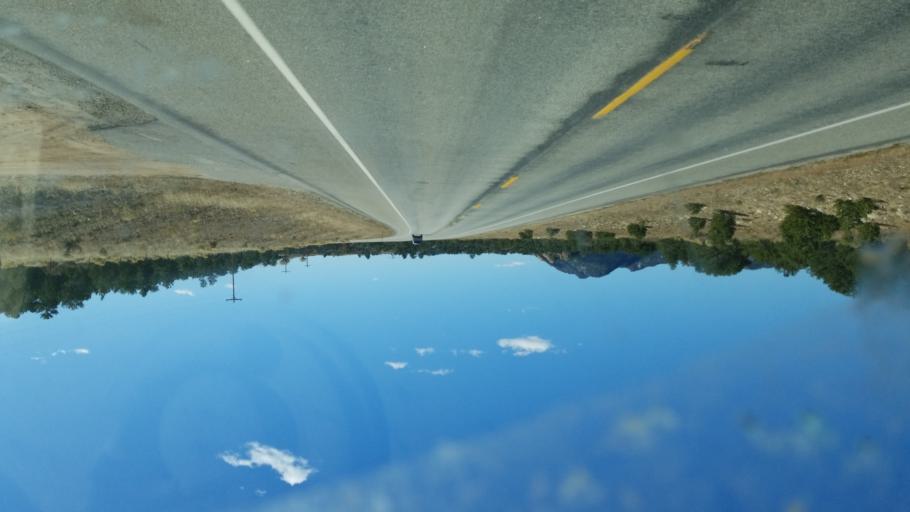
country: US
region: Colorado
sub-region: Chaffee County
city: Buena Vista
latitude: 38.8895
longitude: -106.1687
